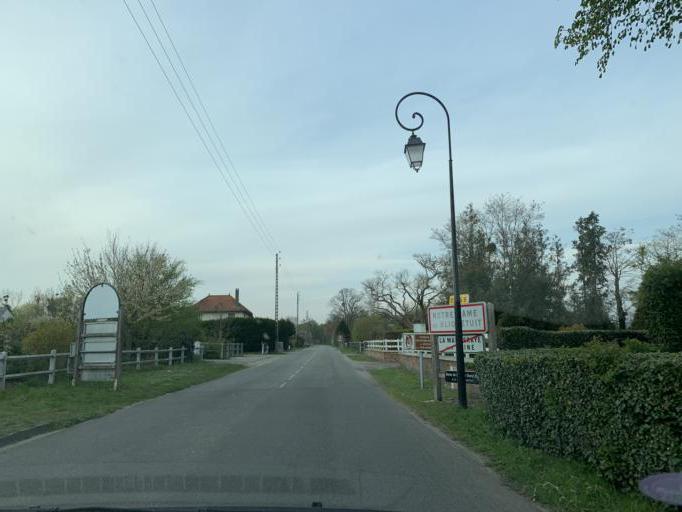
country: FR
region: Haute-Normandie
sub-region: Departement de la Seine-Maritime
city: La Mailleraye-sur-Seine
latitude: 49.4847
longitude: 0.7704
